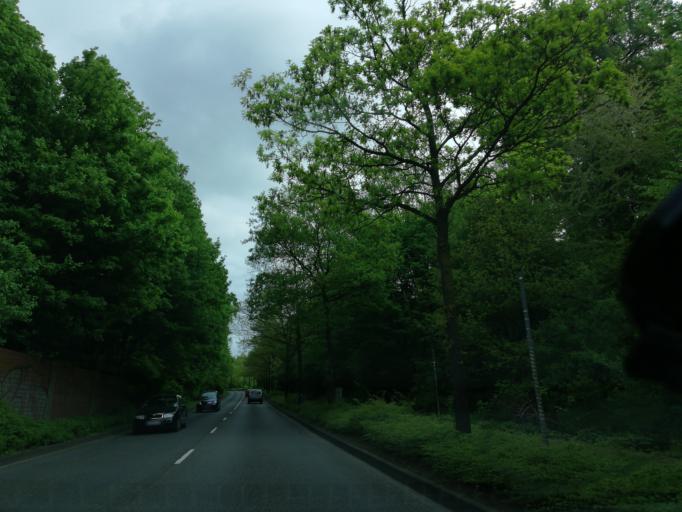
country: DE
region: North Rhine-Westphalia
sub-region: Regierungsbezirk Arnsberg
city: Schwelm
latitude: 51.2894
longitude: 7.2467
